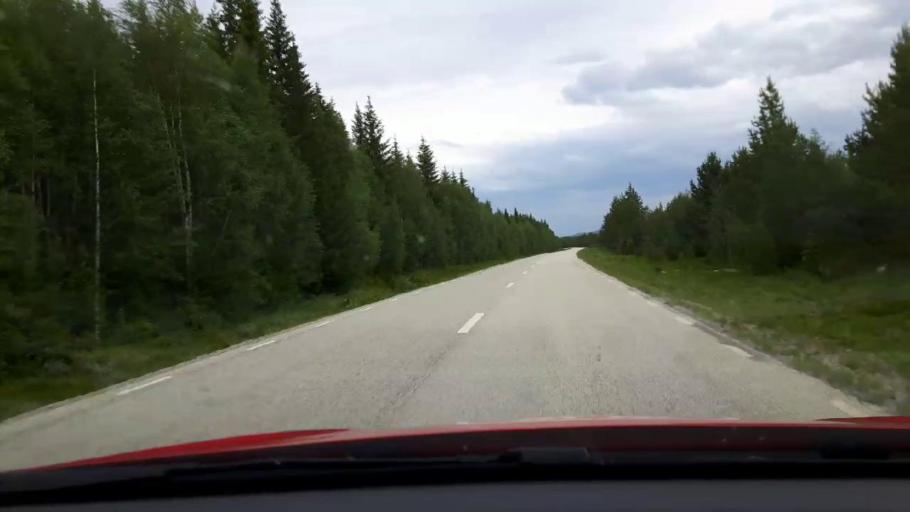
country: SE
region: Jaemtland
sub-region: Bergs Kommun
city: Hoverberg
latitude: 62.7128
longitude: 13.9289
